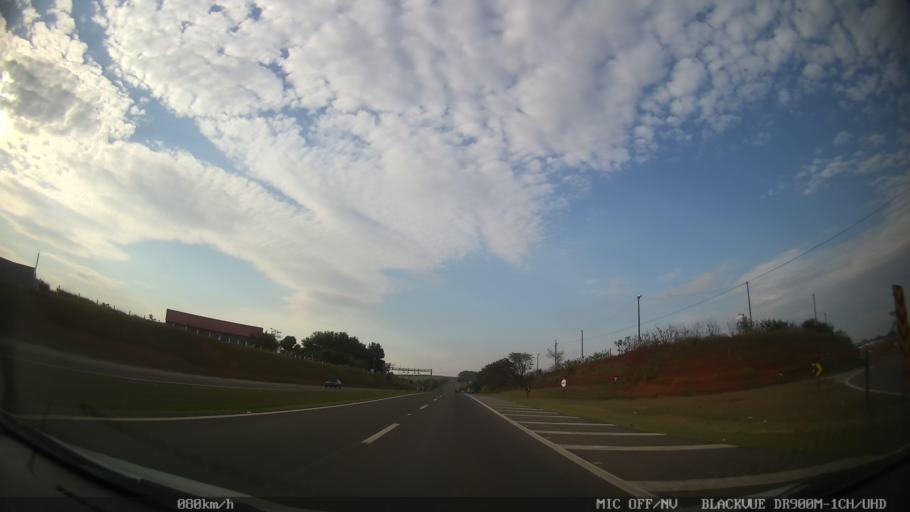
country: BR
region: Sao Paulo
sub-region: Cosmopolis
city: Cosmopolis
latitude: -22.6205
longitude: -47.1995
